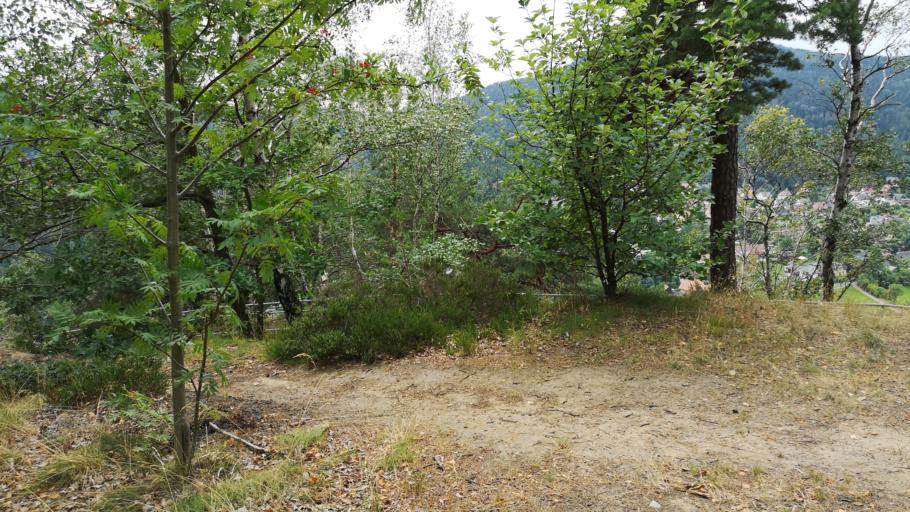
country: DE
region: Saxony
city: Kurort Oybin
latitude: 50.8437
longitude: 14.7422
